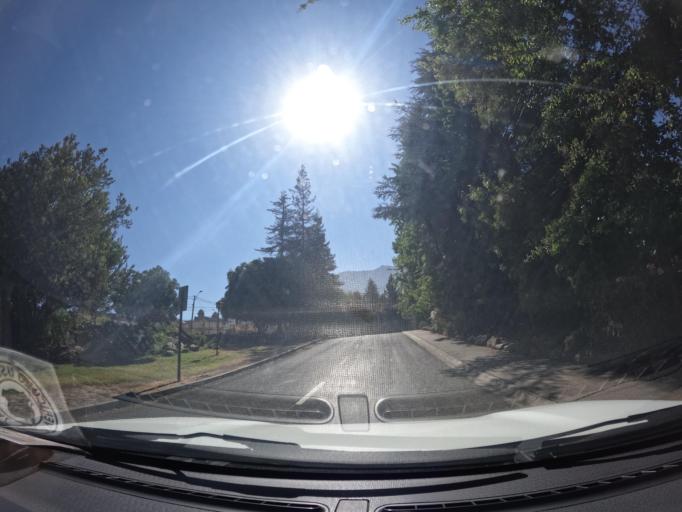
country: CL
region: Santiago Metropolitan
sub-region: Provincia de Santiago
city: Villa Presidente Frei, Nunoa, Santiago, Chile
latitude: -33.4786
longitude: -70.5224
